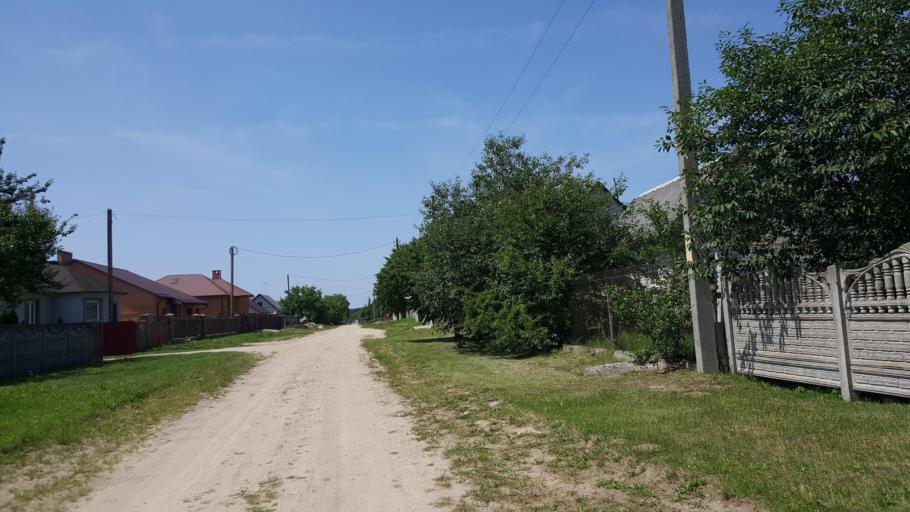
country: BY
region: Brest
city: Vysokaye
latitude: 52.3611
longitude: 23.3938
